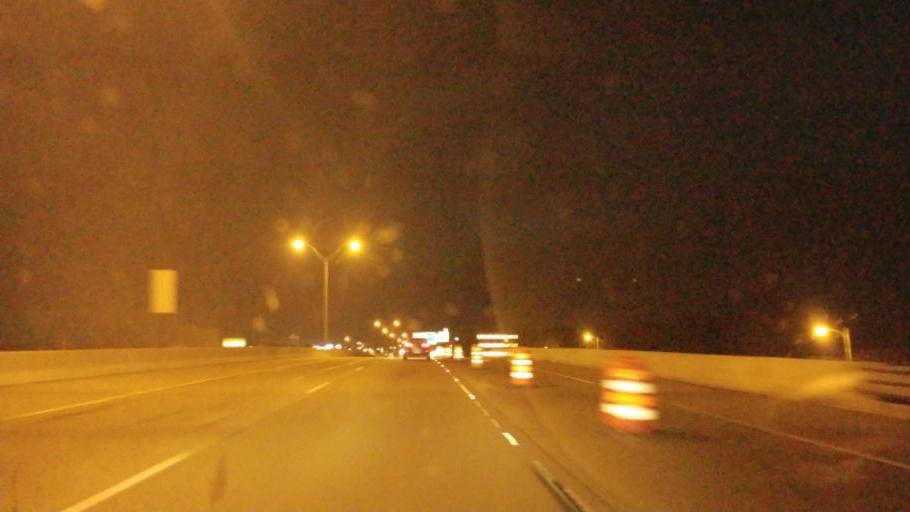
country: US
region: Texas
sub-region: Potter County
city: Amarillo
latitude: 35.1954
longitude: -101.8574
